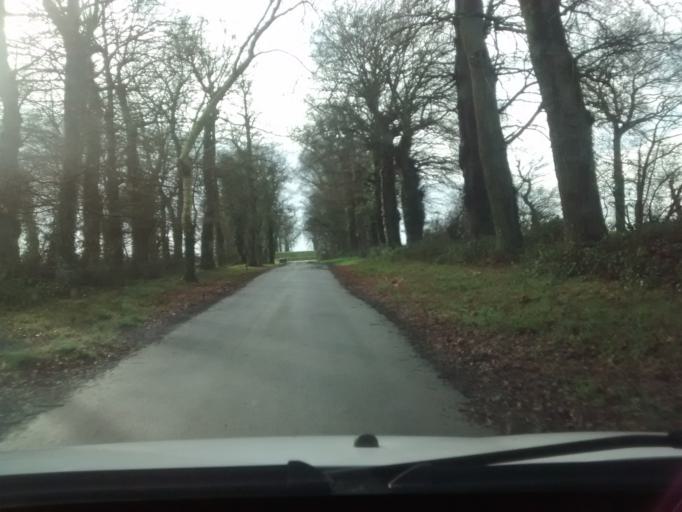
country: FR
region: Brittany
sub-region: Departement d'Ille-et-Vilaine
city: Vezin-le-Coquet
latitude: 48.1276
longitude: -1.7359
